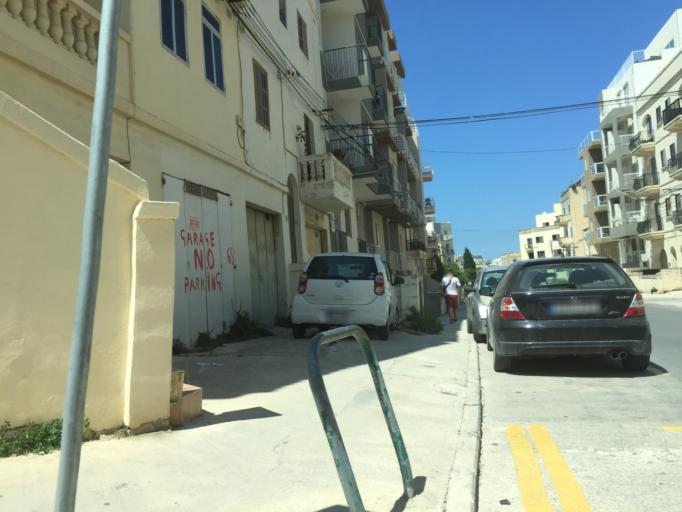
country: MT
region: Ta' Xbiex
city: Ta' Xbiex
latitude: 35.8996
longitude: 14.4884
